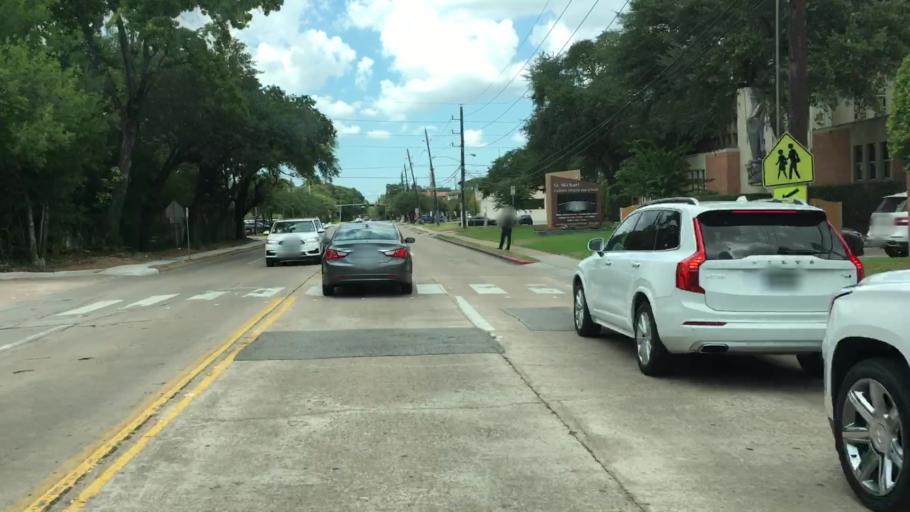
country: US
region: Texas
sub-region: Harris County
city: Hunters Creek Village
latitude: 29.7477
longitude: -95.4671
